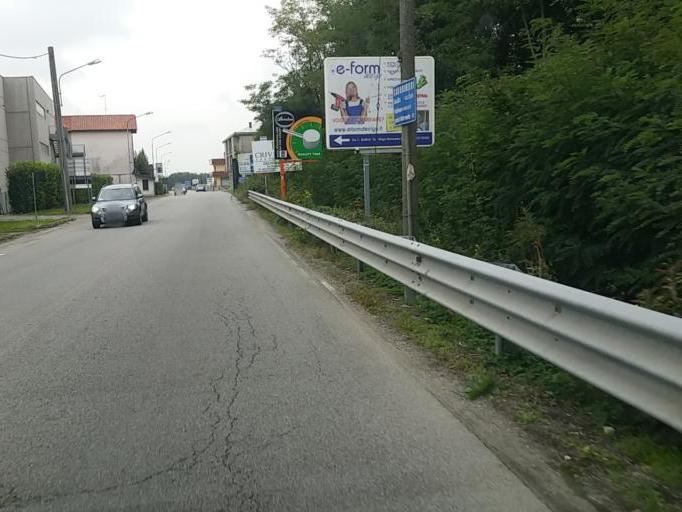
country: IT
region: Piedmont
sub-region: Provincia di Novara
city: Briga Novarese
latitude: 45.7290
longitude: 8.4440
